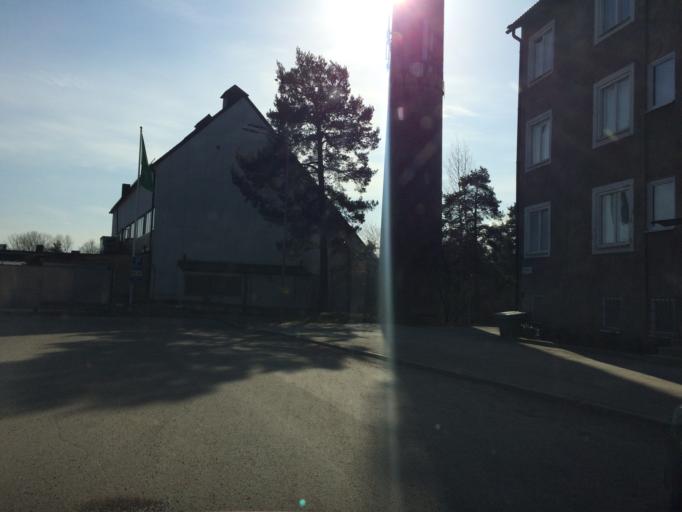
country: SE
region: Stockholm
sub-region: Stockholms Kommun
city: Arsta
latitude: 59.2898
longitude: 18.0036
